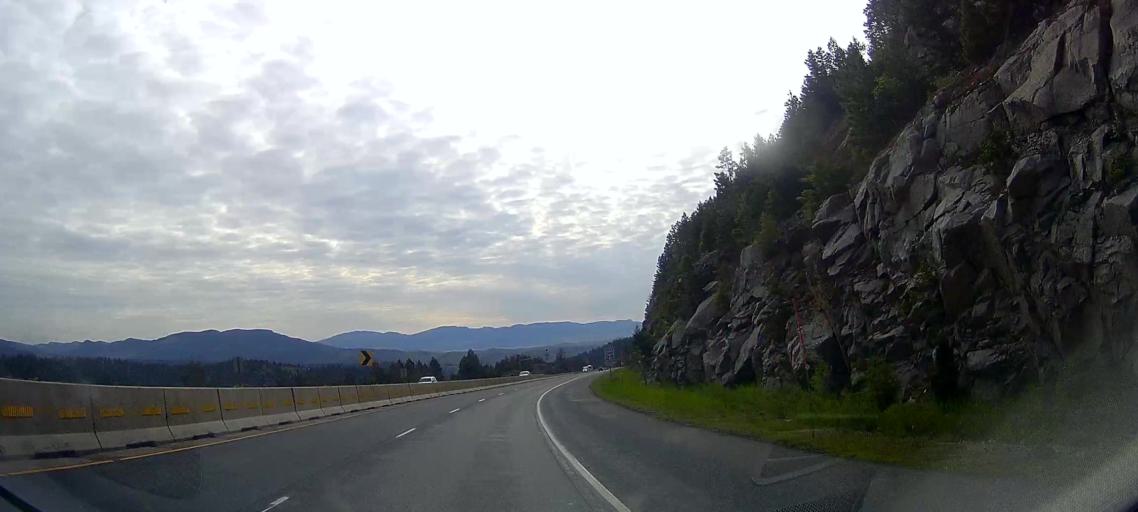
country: US
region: Montana
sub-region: Jefferson County
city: Whitehall
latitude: 45.9099
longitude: -112.3191
